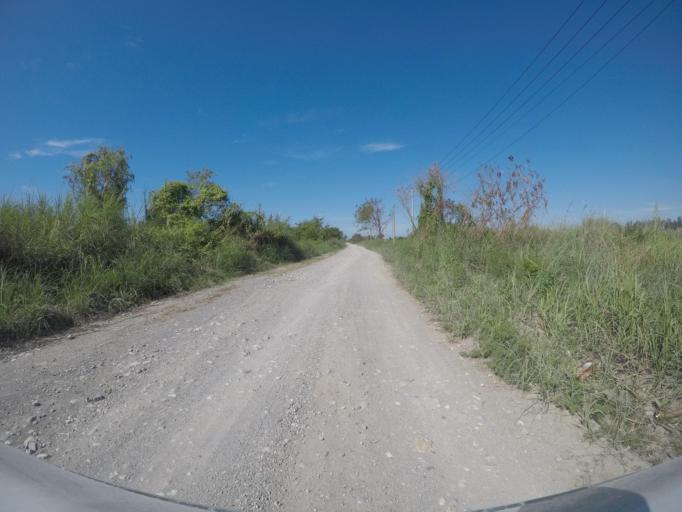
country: TL
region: Viqueque
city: Viqueque
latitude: -8.9411
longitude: 126.1142
